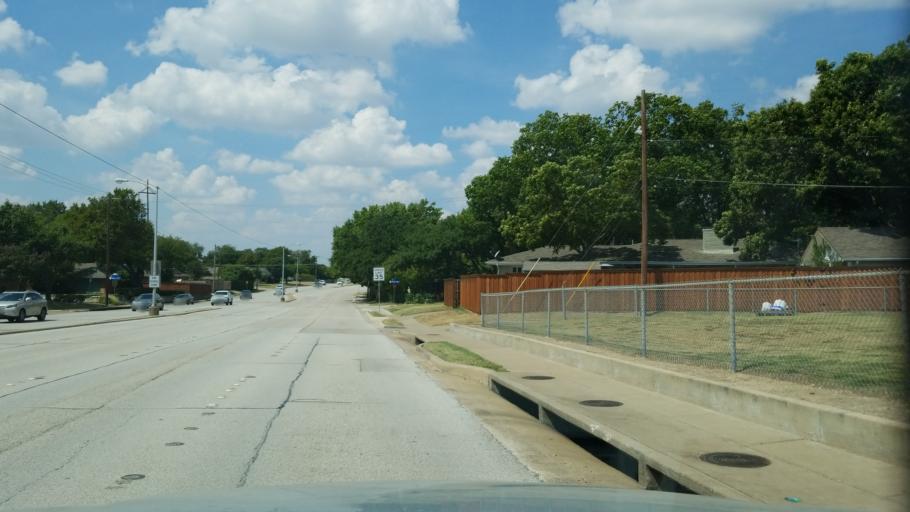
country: US
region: Texas
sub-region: Dallas County
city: Richardson
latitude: 32.9510
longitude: -96.7465
